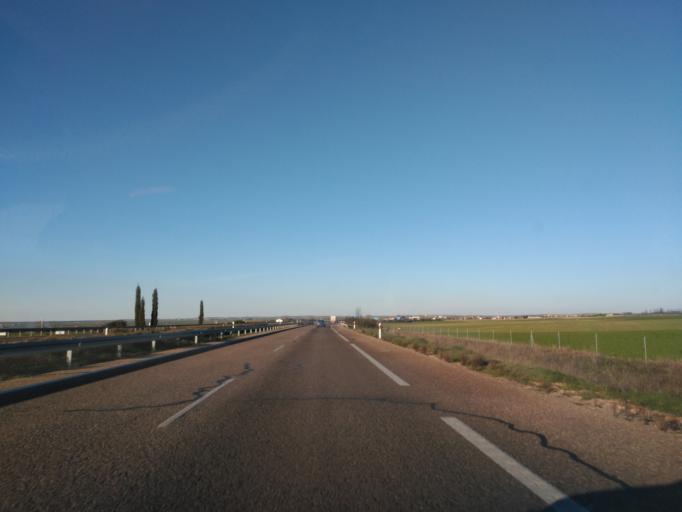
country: ES
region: Castille and Leon
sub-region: Provincia de Salamanca
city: Pedrosillo el Ralo
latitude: 41.0428
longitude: -5.5591
